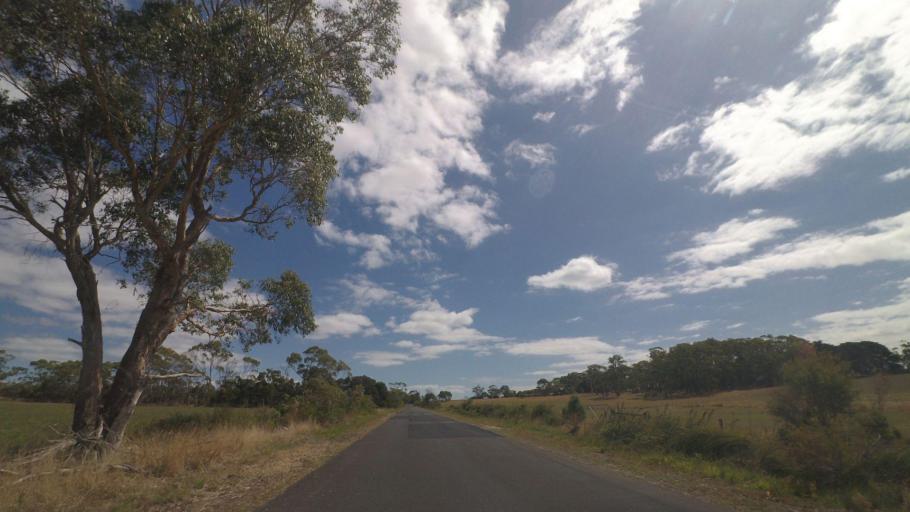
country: AU
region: Victoria
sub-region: Cardinia
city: Bunyip
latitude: -38.3159
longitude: 145.7386
